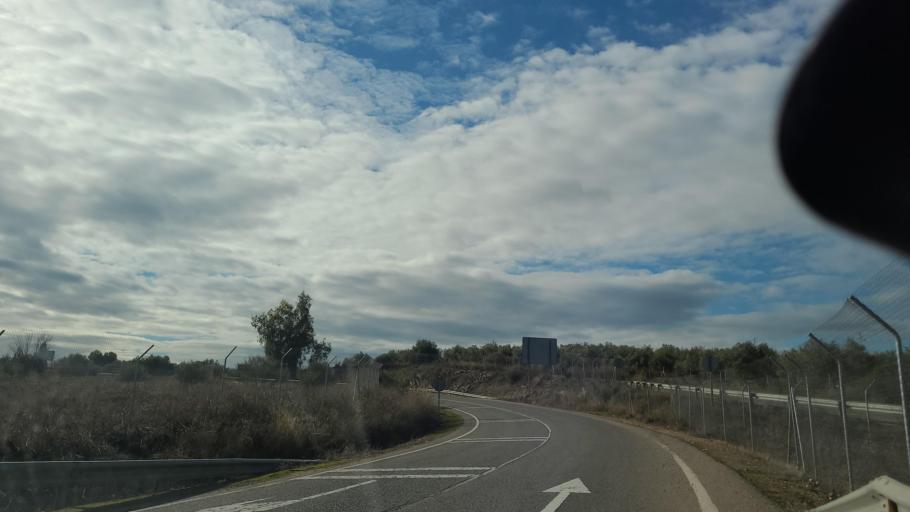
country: ES
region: Andalusia
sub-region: Provincia de Jaen
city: Villanueva de la Reina
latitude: 38.0507
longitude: -3.9067
